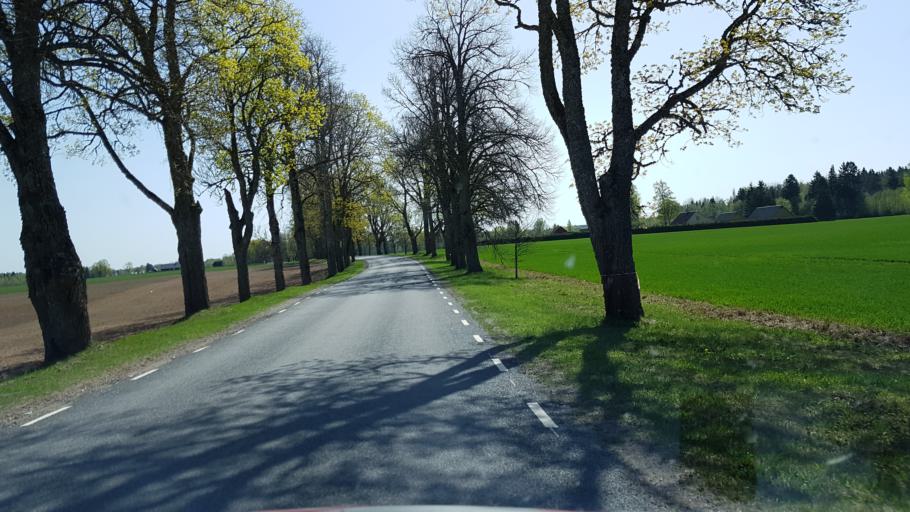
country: EE
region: Viljandimaa
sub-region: Vohma linn
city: Vohma
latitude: 58.5444
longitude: 25.5699
